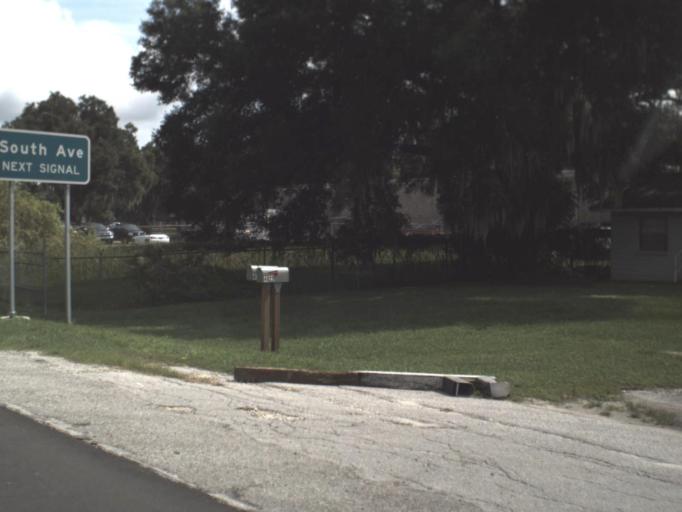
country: US
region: Florida
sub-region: Pasco County
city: Zephyrhills
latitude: 28.2278
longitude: -82.1800
